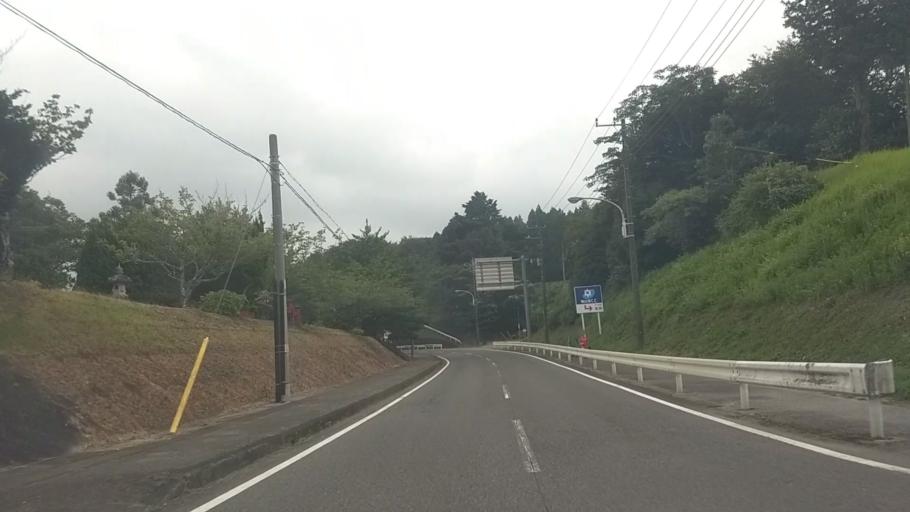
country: JP
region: Chiba
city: Kawaguchi
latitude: 35.2289
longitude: 140.0894
